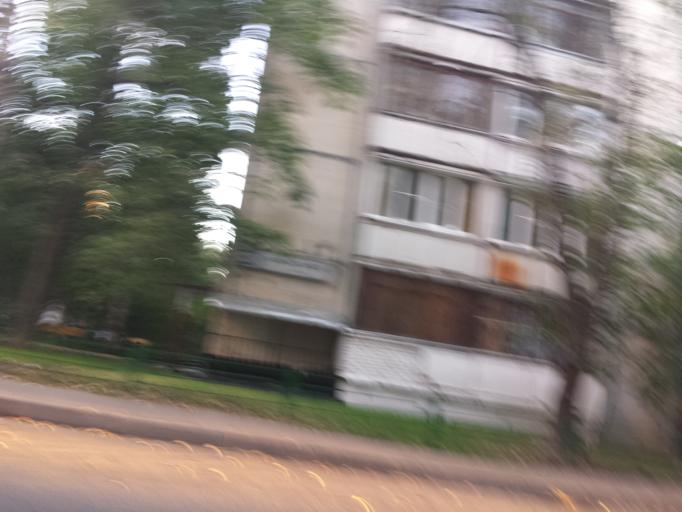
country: RU
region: Moskovskaya
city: Novogireyevo
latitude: 55.7475
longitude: 37.8135
